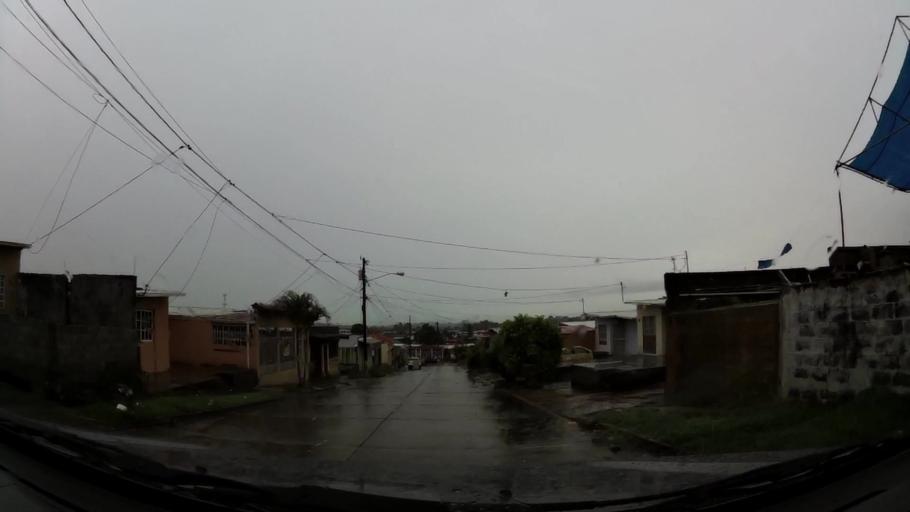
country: PA
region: Colon
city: Puerto Pilon
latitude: 9.3552
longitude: -79.7911
